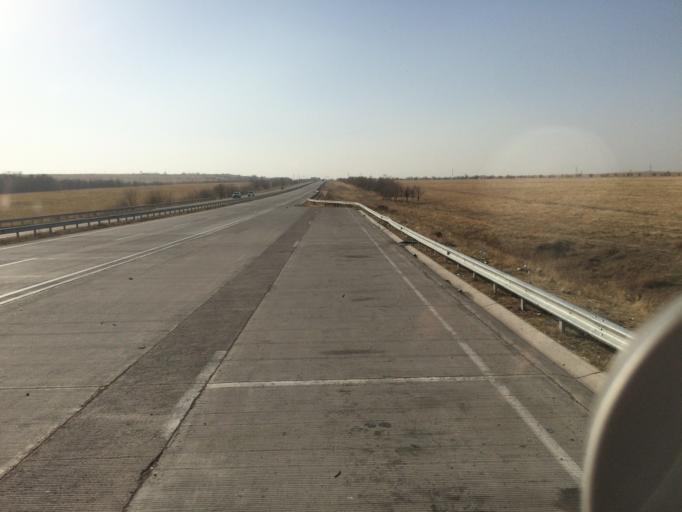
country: KZ
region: Zhambyl
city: Sarykemer
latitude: 43.0101
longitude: 71.6587
